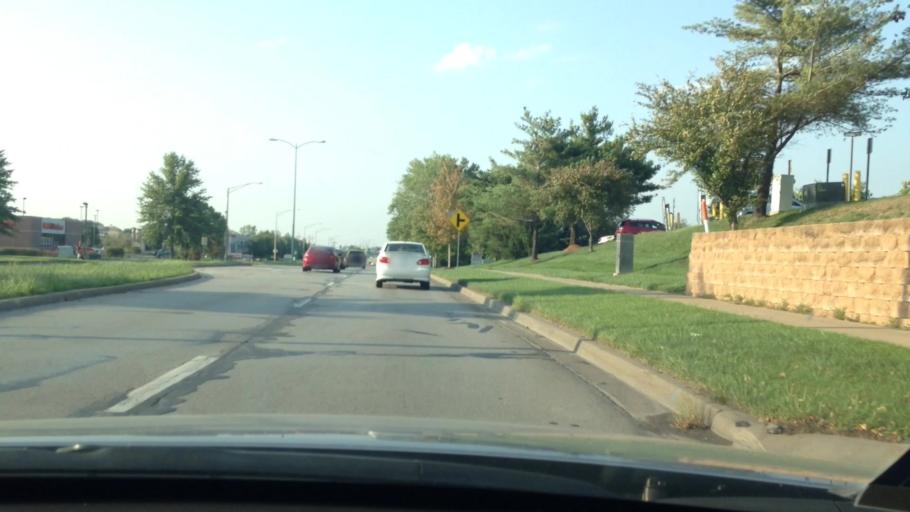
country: US
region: Missouri
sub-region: Platte County
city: Weatherby Lake
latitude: 39.2490
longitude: -94.6496
